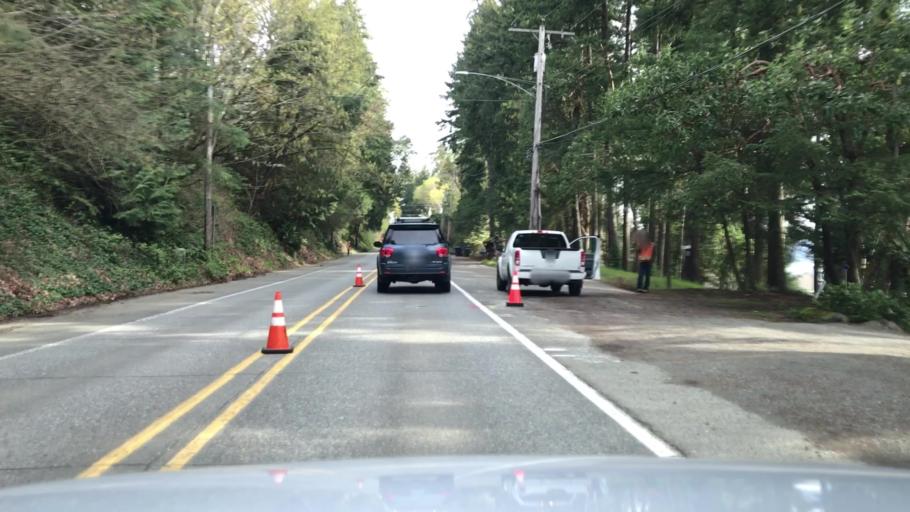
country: US
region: Washington
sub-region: King County
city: West Lake Sammamish
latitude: 47.5962
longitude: -122.1110
